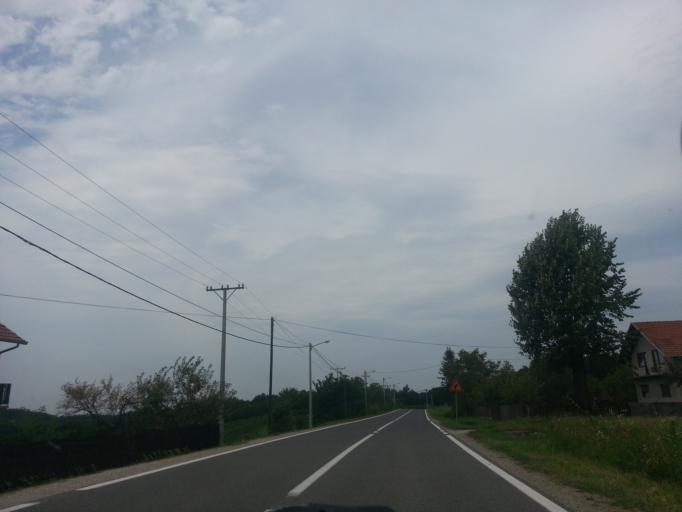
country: BA
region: Brcko
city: Brcko
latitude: 44.8009
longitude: 18.8106
